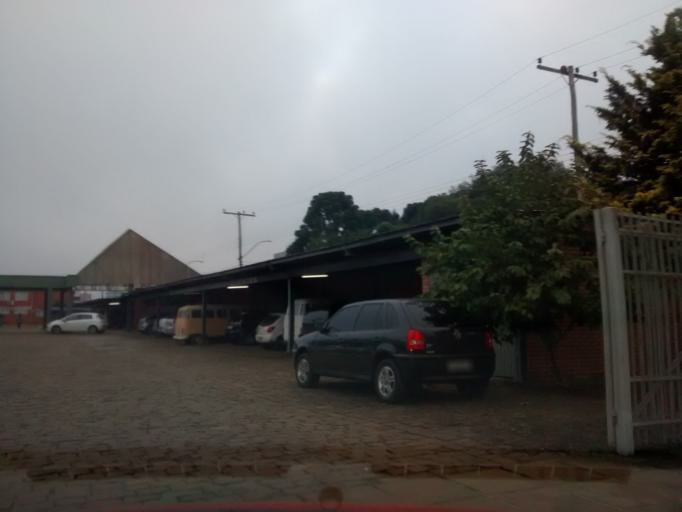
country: BR
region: Rio Grande do Sul
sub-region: Vacaria
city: Vacaria
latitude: -28.5079
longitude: -50.9443
